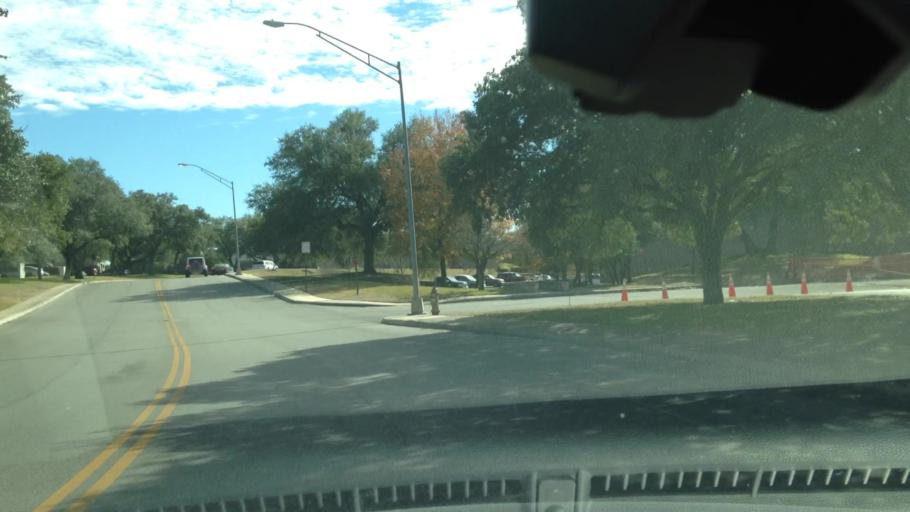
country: US
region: Texas
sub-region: Bexar County
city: Shavano Park
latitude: 29.5533
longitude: -98.5909
